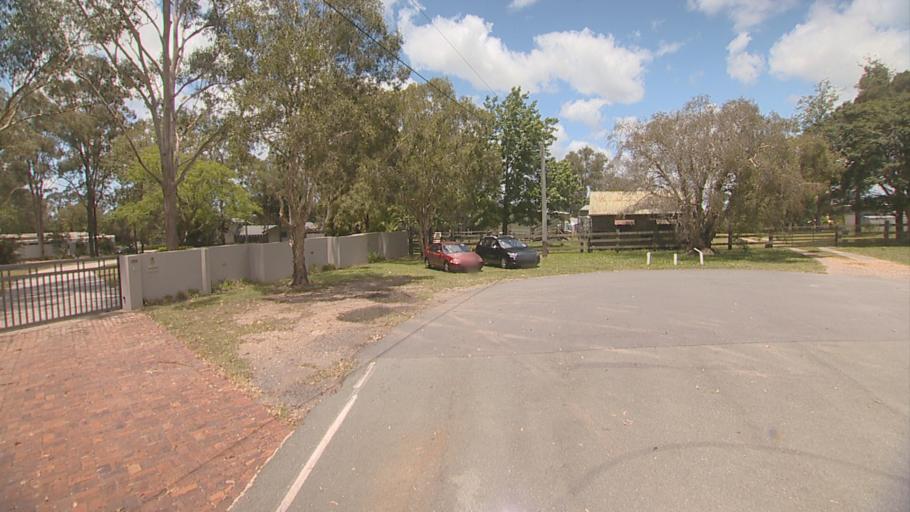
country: AU
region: Queensland
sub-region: Gold Coast
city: Yatala
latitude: -27.6811
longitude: 153.2358
